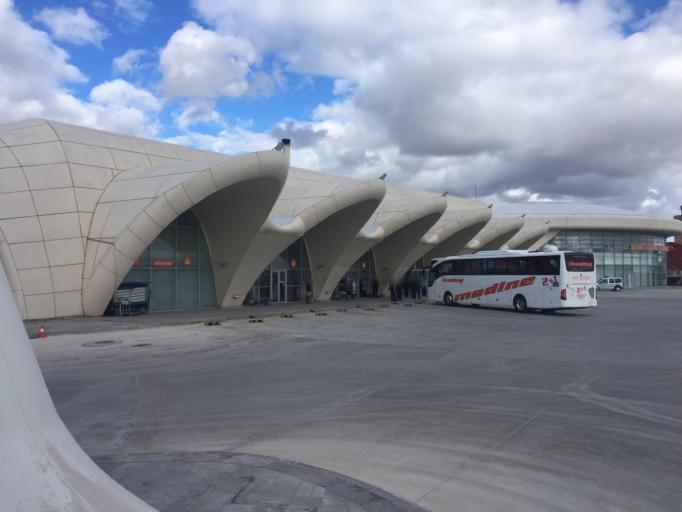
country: TR
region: Kirsehir
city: Kirsehir
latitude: 39.1705
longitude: 34.1486
